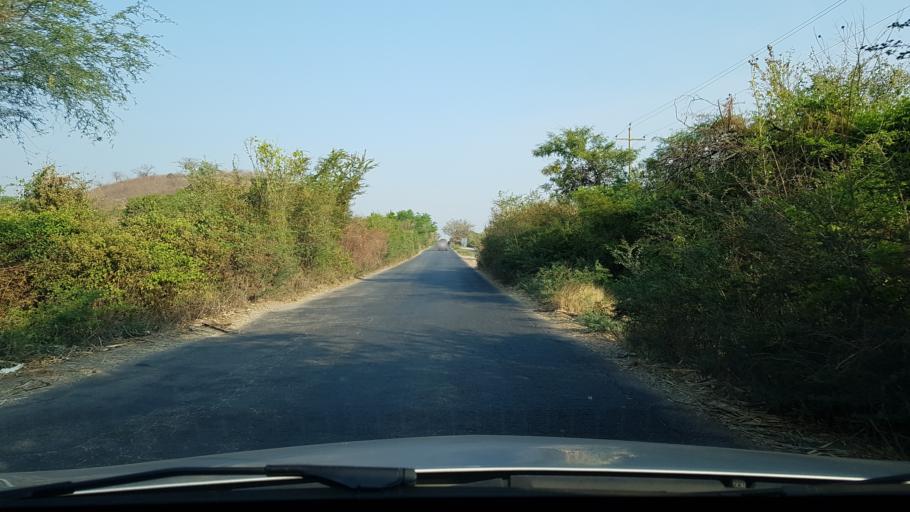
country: MX
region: Morelos
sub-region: Tepalcingo
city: Zacapalco
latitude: 18.6417
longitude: -99.0188
